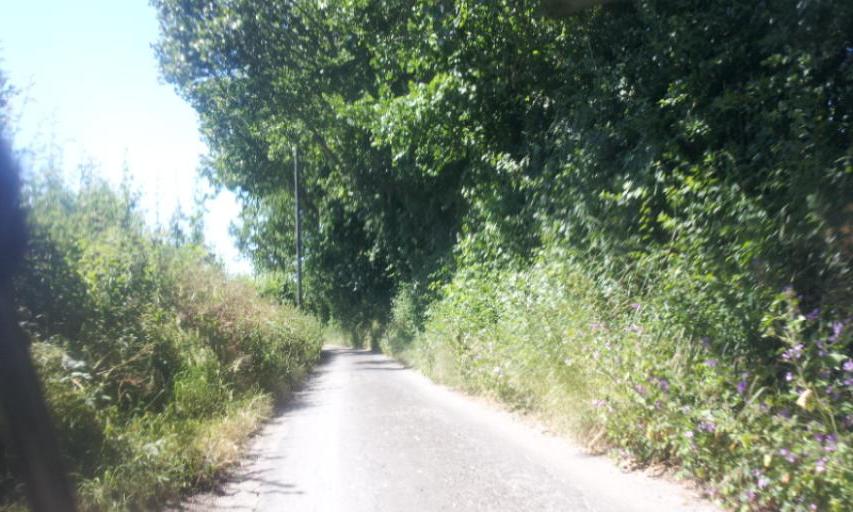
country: GB
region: England
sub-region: Kent
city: Teynham
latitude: 51.3531
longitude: 0.7787
